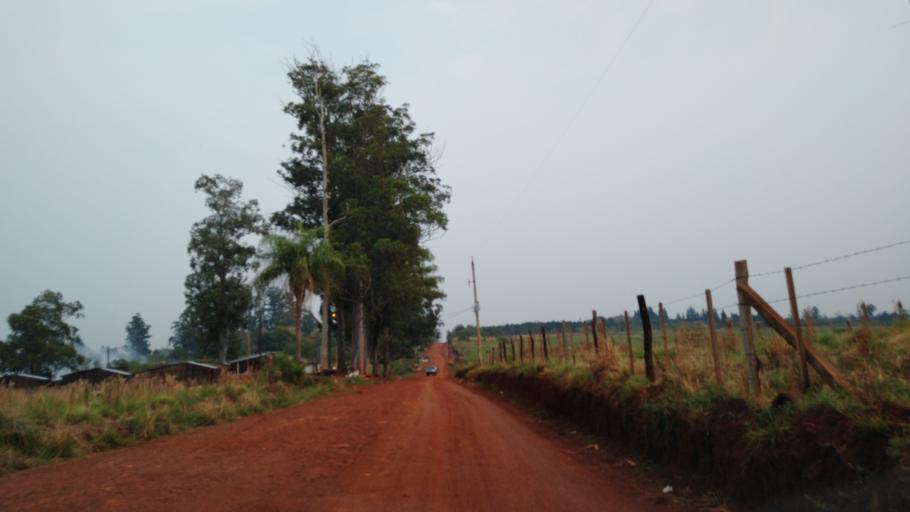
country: AR
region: Misiones
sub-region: Departamento de Capital
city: Posadas
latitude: -27.4475
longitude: -55.9361
